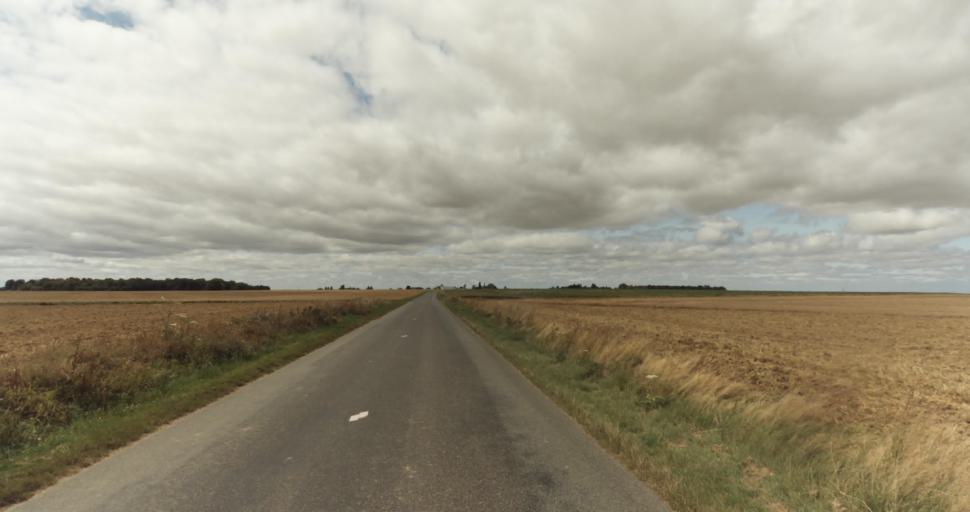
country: FR
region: Haute-Normandie
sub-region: Departement de l'Eure
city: Evreux
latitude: 48.9118
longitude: 1.2341
